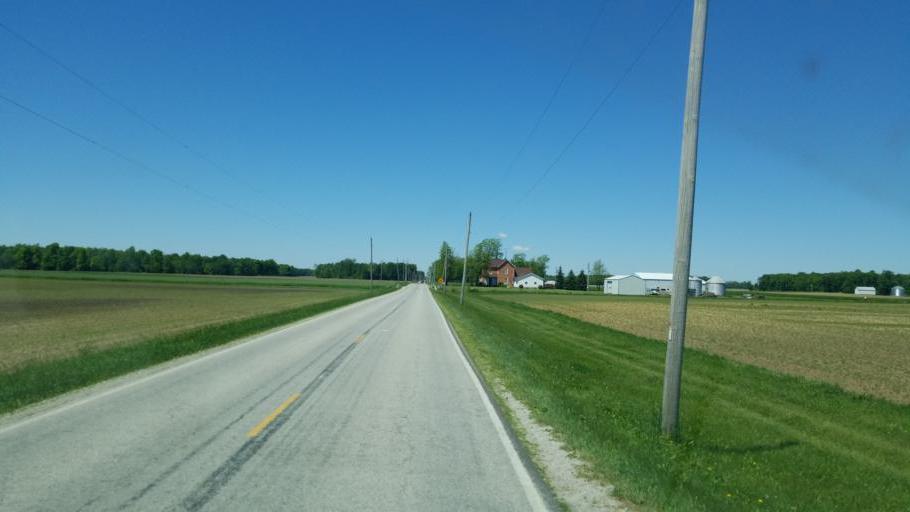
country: US
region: Ohio
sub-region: Shelby County
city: Fort Loramie
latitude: 40.3560
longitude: -84.3194
